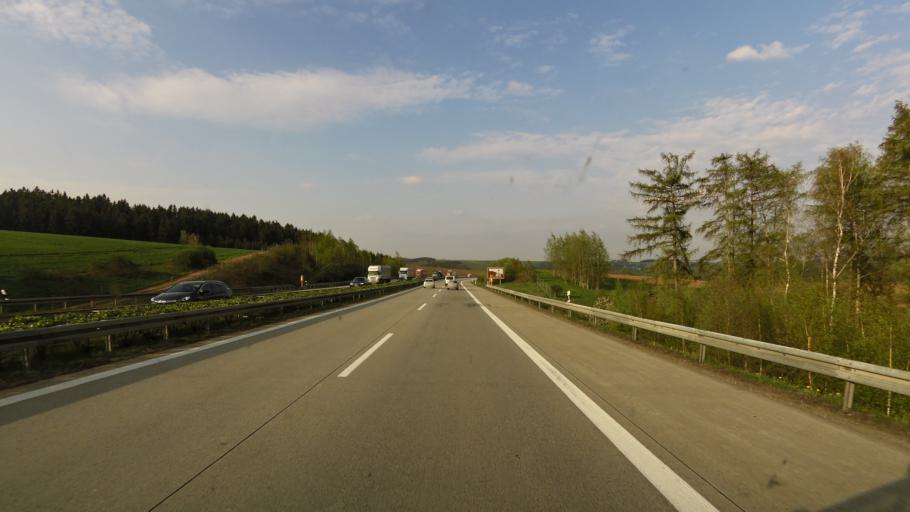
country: DE
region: Saxony
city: Hartenstein
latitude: 50.6862
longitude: 12.6524
